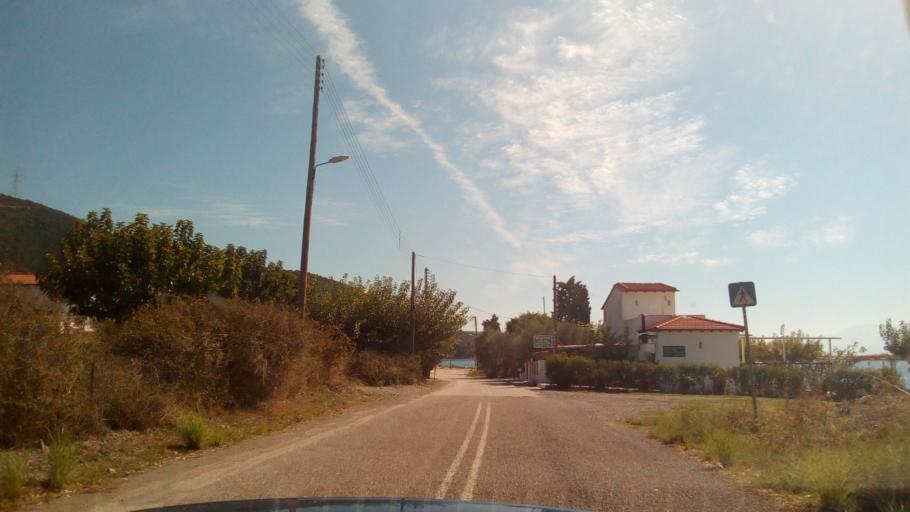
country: GR
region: West Greece
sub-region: Nomos Achaias
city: Selianitika
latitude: 38.3741
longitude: 22.0879
